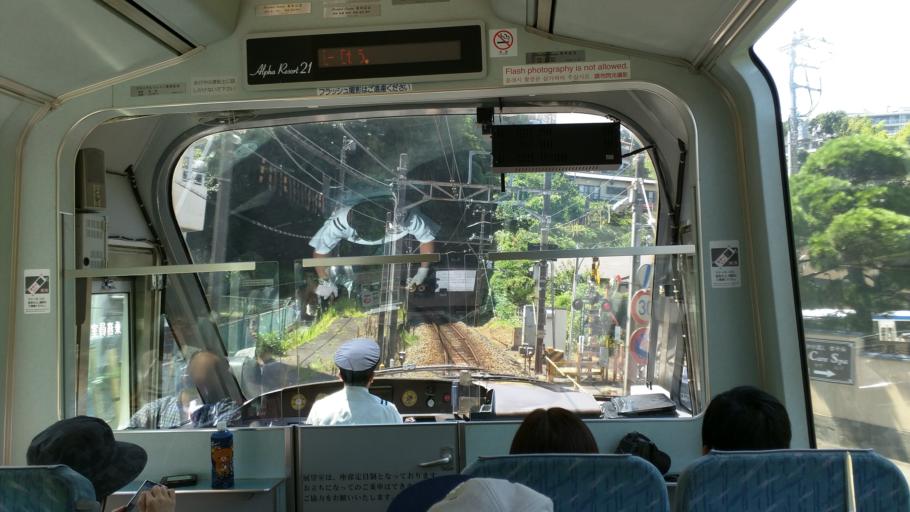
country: JP
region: Shizuoka
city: Ito
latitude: 34.9680
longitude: 139.0891
